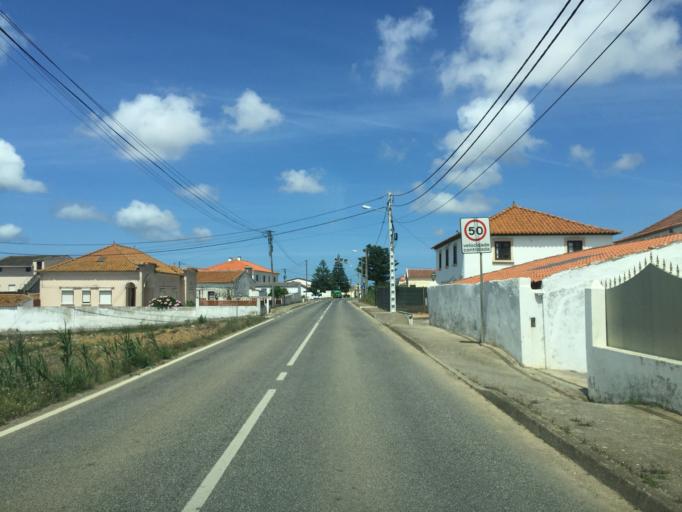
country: PT
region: Lisbon
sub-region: Lourinha
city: Lourinha
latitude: 39.2791
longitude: -9.2999
